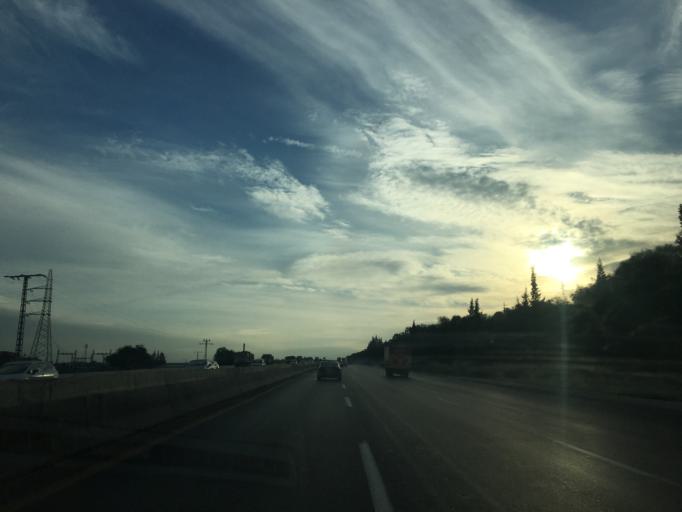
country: DZ
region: Bouira
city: Draa el Mizan
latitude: 36.4749
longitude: 3.7526
